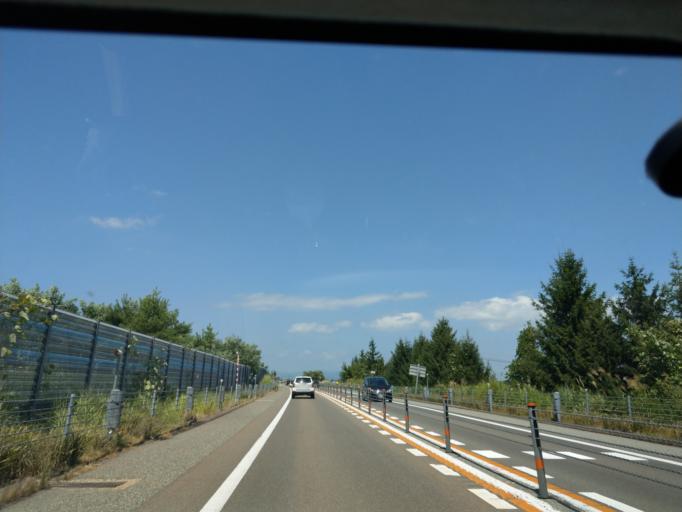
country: JP
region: Akita
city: Omagari
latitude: 39.3903
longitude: 140.4787
